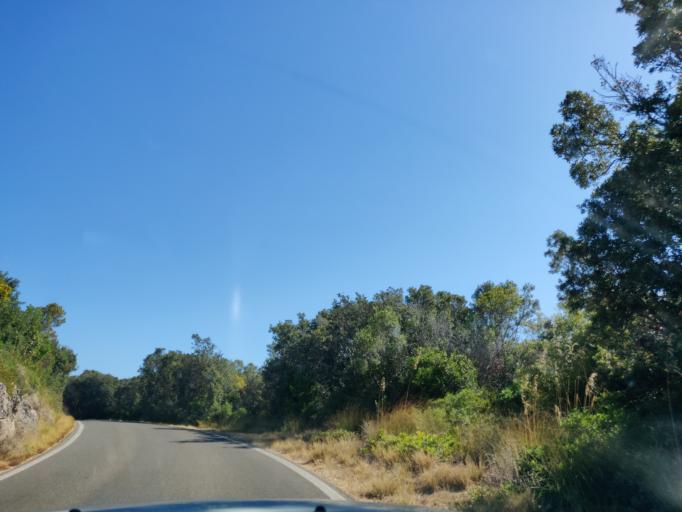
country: IT
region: Tuscany
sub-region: Provincia di Grosseto
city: Porto Ercole
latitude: 42.4284
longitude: 11.1718
